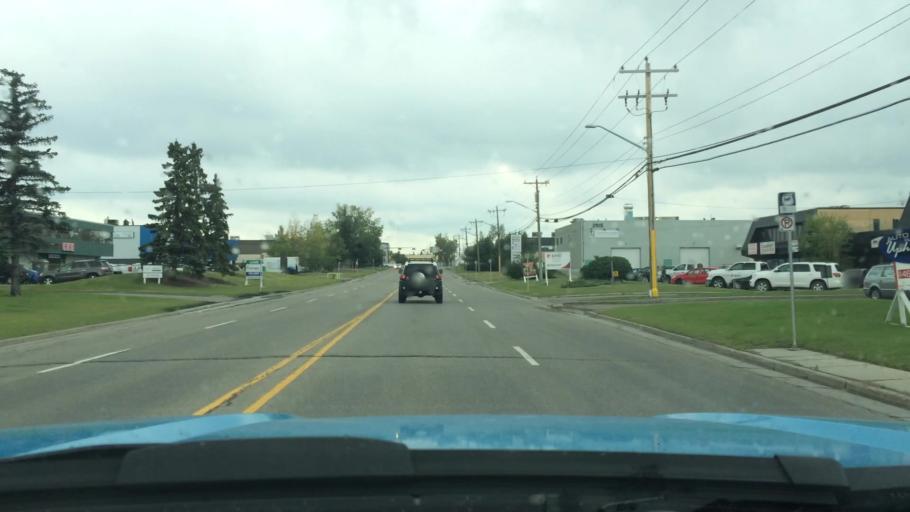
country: CA
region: Alberta
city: Calgary
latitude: 51.0794
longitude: -114.0117
